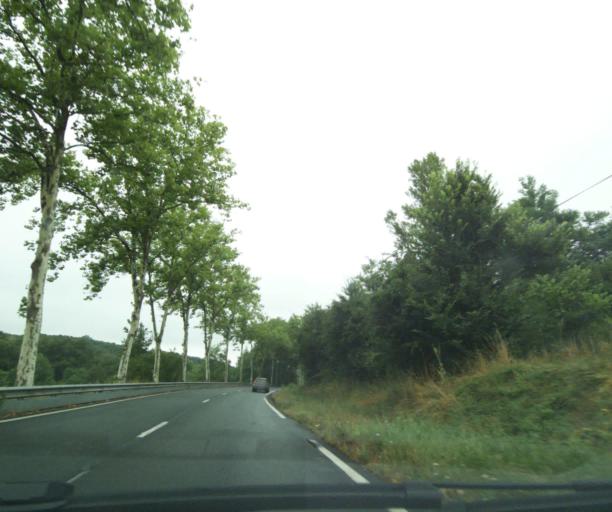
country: FR
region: Midi-Pyrenees
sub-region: Departement du Tarn
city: Le Garric
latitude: 43.9826
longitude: 2.1737
